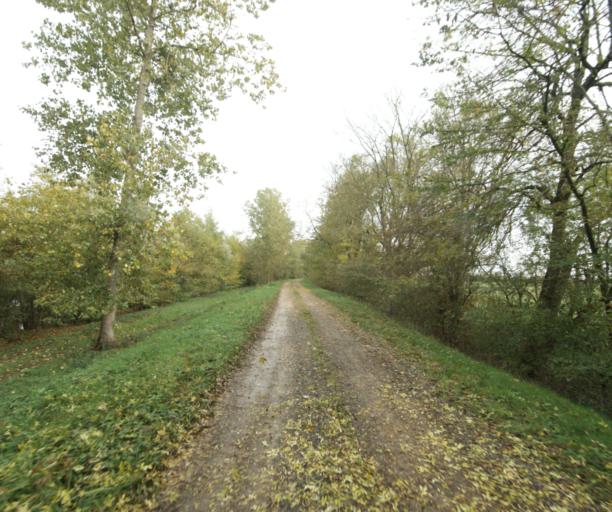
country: FR
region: Rhone-Alpes
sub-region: Departement de l'Ain
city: Pont-de-Vaux
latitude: 46.4561
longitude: 4.8983
